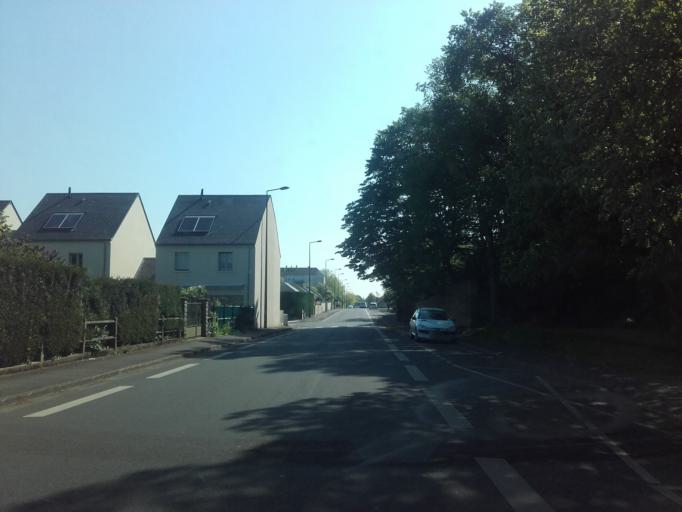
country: FR
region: Centre
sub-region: Departement d'Indre-et-Loire
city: Saint-Cyr-sur-Loire
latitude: 47.4256
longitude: 0.6789
